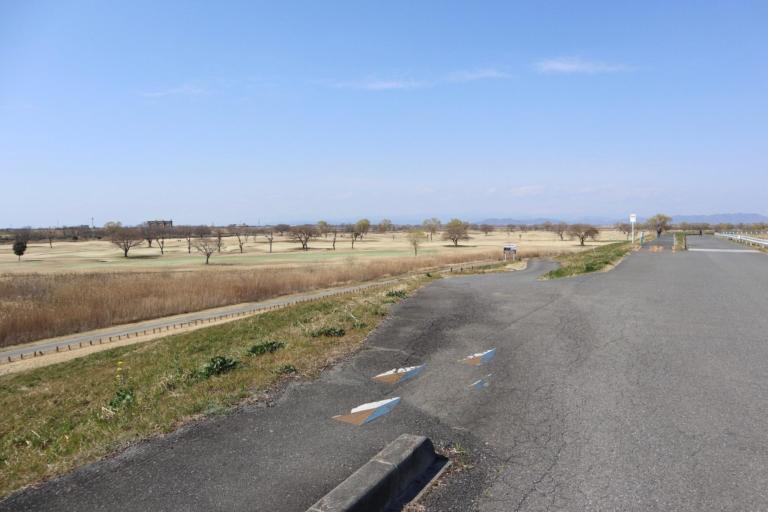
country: JP
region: Ibaraki
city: Koga
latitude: 36.1947
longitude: 139.6950
